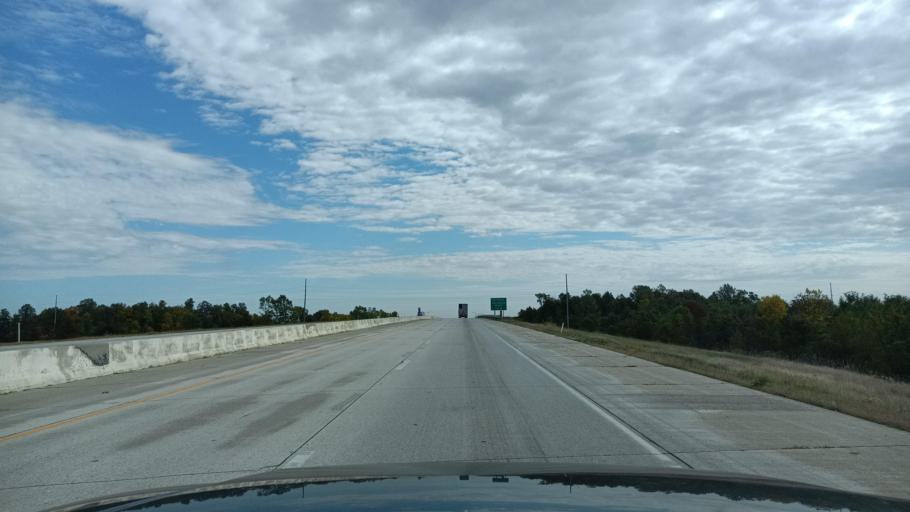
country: US
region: Indiana
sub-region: Wells County
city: Ossian
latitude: 40.9536
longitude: -85.1816
